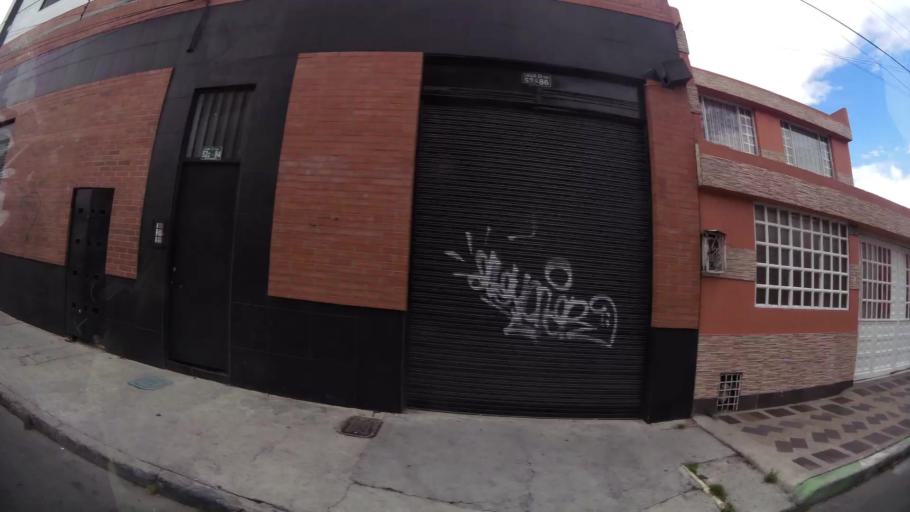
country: CO
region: Bogota D.C.
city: Bogota
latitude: 4.6059
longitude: -74.1306
